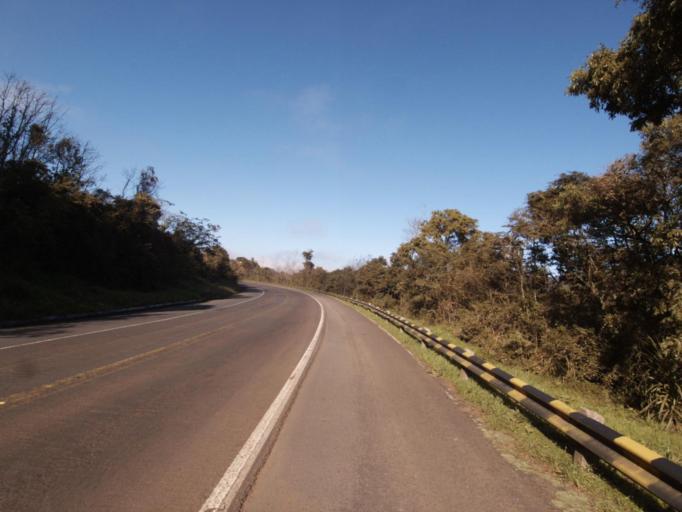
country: BR
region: Rio Grande do Sul
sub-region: Frederico Westphalen
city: Frederico Westphalen
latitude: -26.9871
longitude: -53.2267
